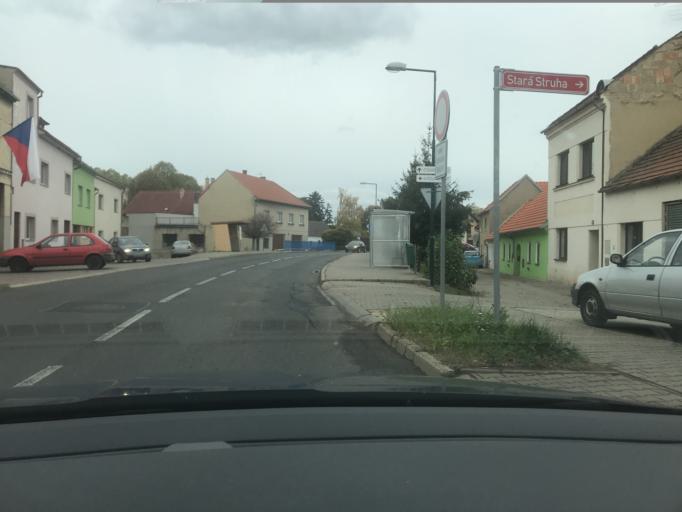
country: CZ
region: Ustecky
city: Trebenice
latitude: 50.4773
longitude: 13.9950
